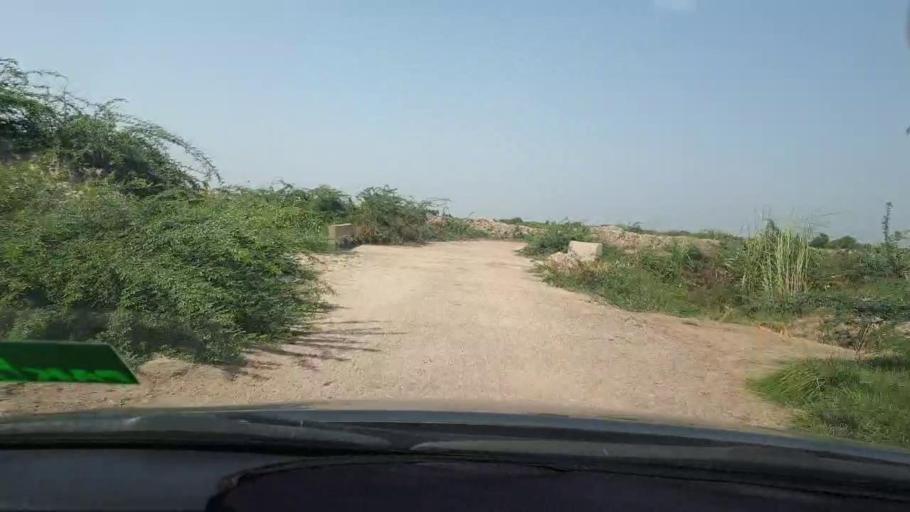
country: PK
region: Sindh
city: Digri
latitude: 24.9421
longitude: 69.1448
